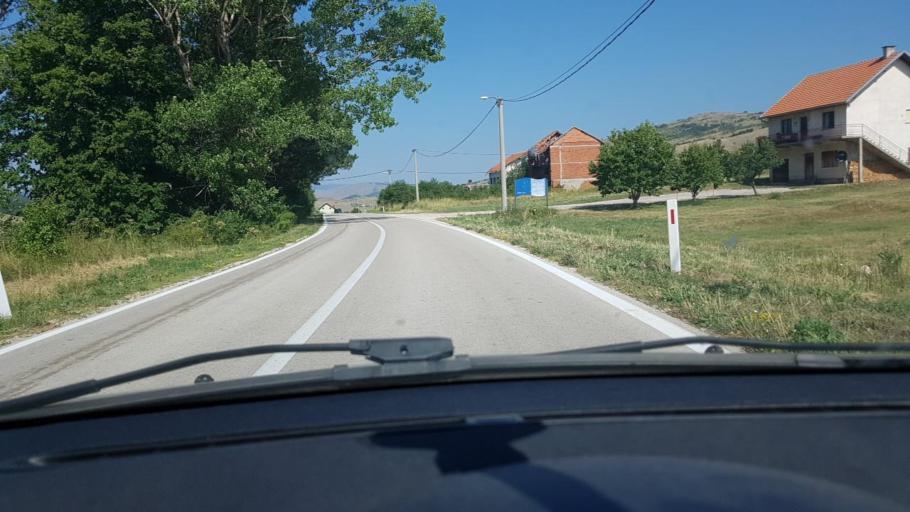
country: BA
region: Federation of Bosnia and Herzegovina
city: Bosansko Grahovo
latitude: 44.1202
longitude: 16.5341
